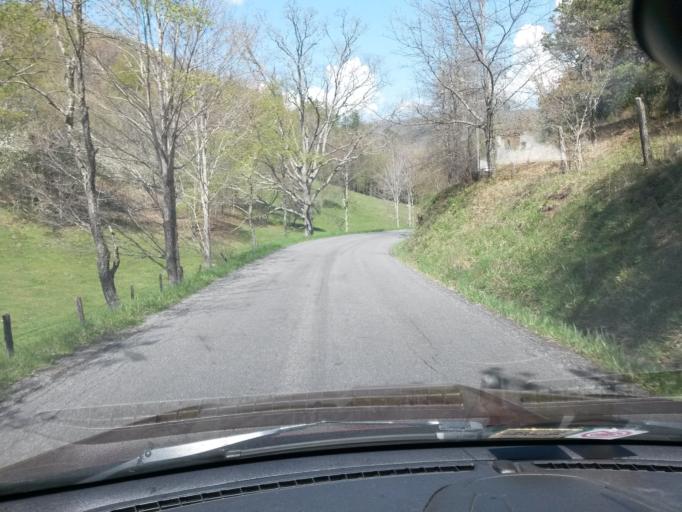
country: US
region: Virginia
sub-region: Highland County
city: Monterey
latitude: 38.3196
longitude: -79.6347
